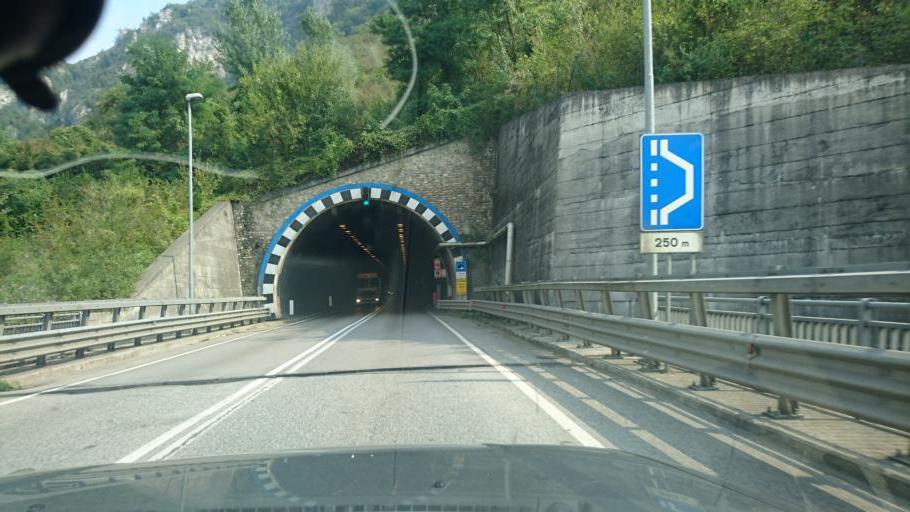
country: IT
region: Lombardy
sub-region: Provincia di Brescia
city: Vobarno
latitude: 45.6429
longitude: 10.4661
